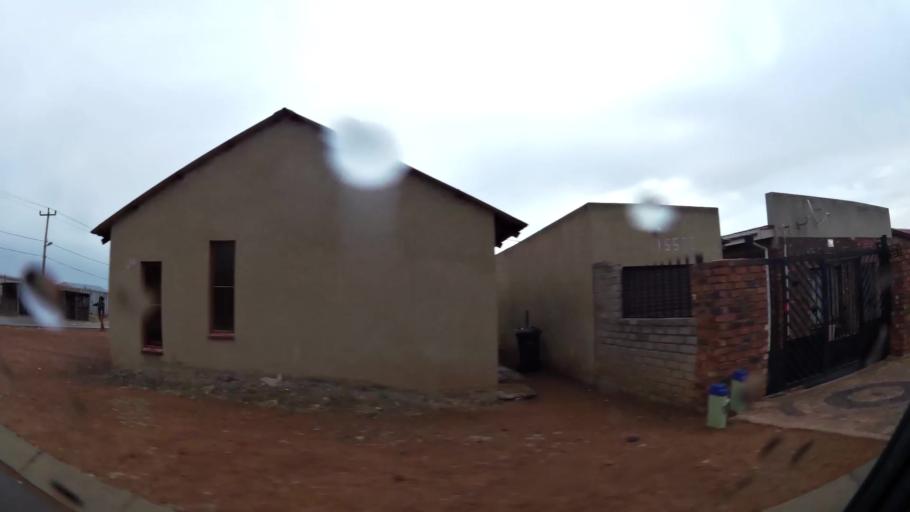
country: ZA
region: Gauteng
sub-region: City of Johannesburg Metropolitan Municipality
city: Roodepoort
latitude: -26.1738
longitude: 27.7898
